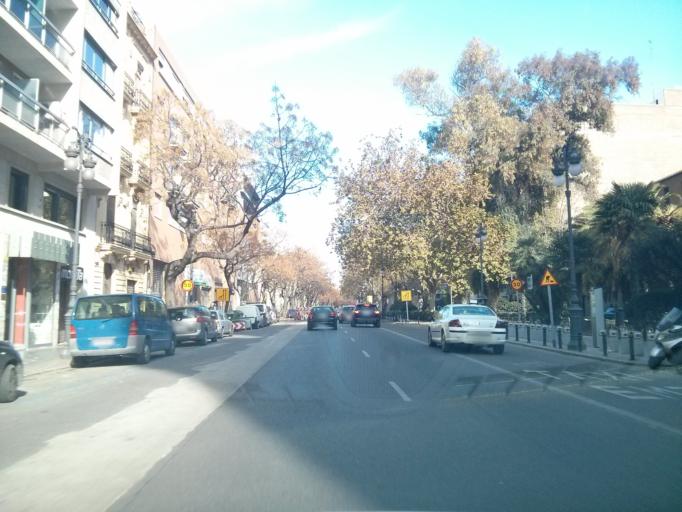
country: ES
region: Valencia
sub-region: Provincia de Valencia
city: Valencia
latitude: 39.4759
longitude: -0.3840
